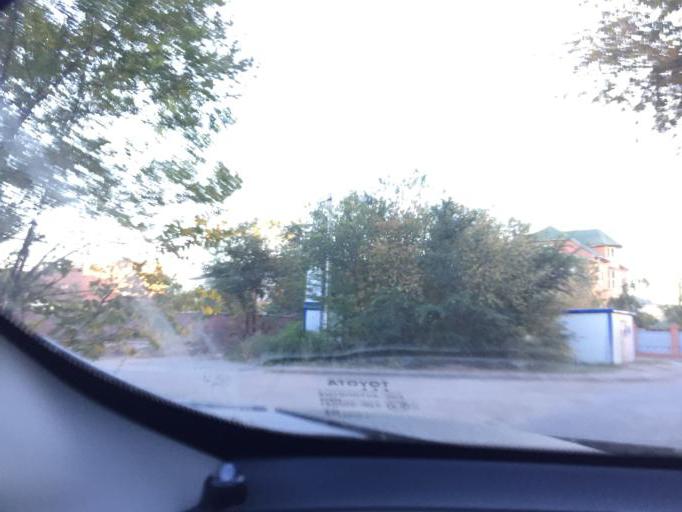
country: KZ
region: Astana Qalasy
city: Astana
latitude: 51.1471
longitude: 71.4273
